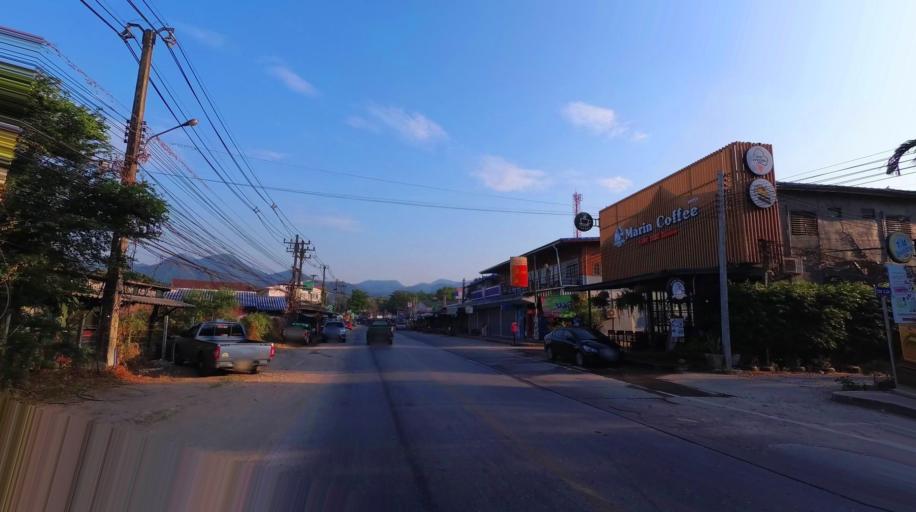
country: TH
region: Trat
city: Ko Chang Tai
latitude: 12.0462
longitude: 102.2985
